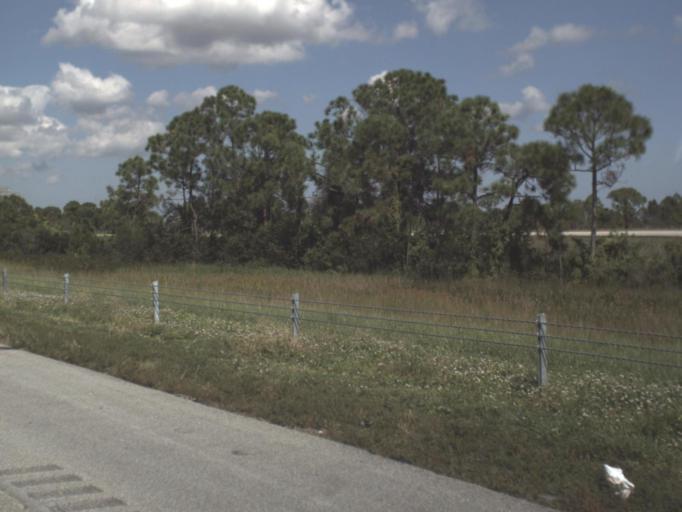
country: US
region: Florida
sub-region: Palm Beach County
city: Limestone Creek
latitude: 26.9485
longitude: -80.1612
